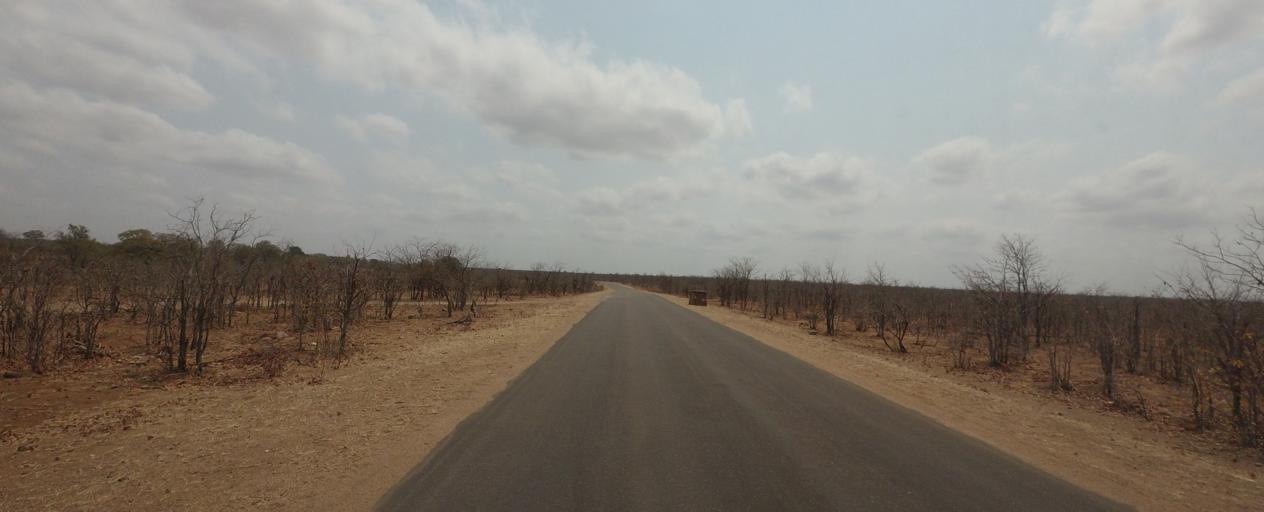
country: ZA
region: Limpopo
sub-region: Mopani District Municipality
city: Phalaborwa
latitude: -23.5464
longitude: 31.4284
